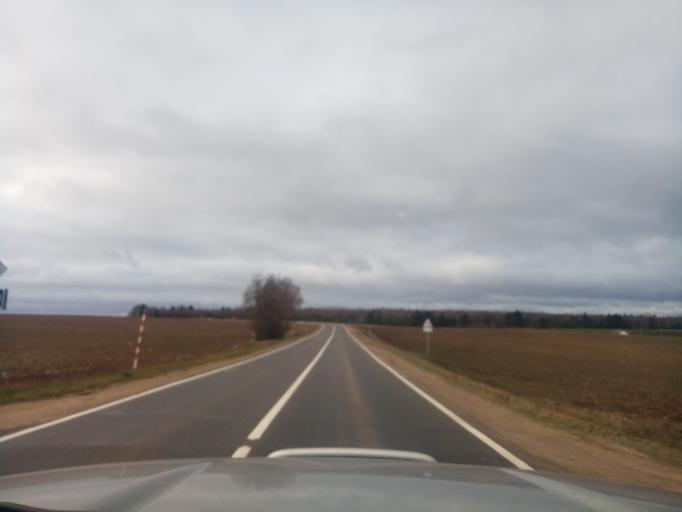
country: BY
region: Minsk
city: Kapyl'
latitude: 53.2082
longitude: 27.2298
